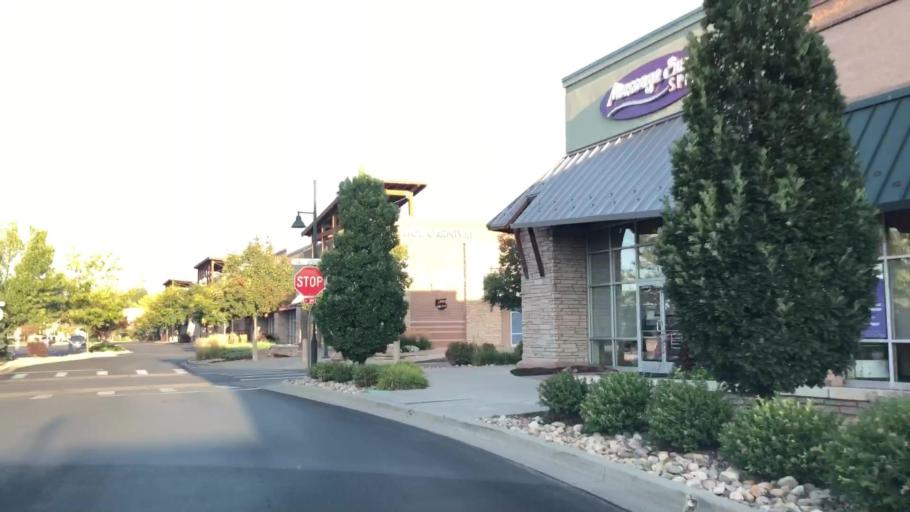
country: US
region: Colorado
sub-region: Larimer County
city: Loveland
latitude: 40.4093
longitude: -105.0067
